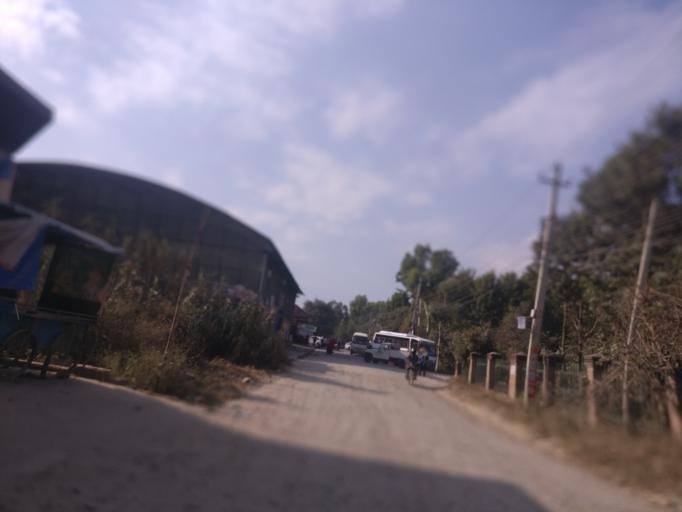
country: NP
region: Central Region
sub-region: Bagmati Zone
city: Patan
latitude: 27.6843
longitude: 85.3272
